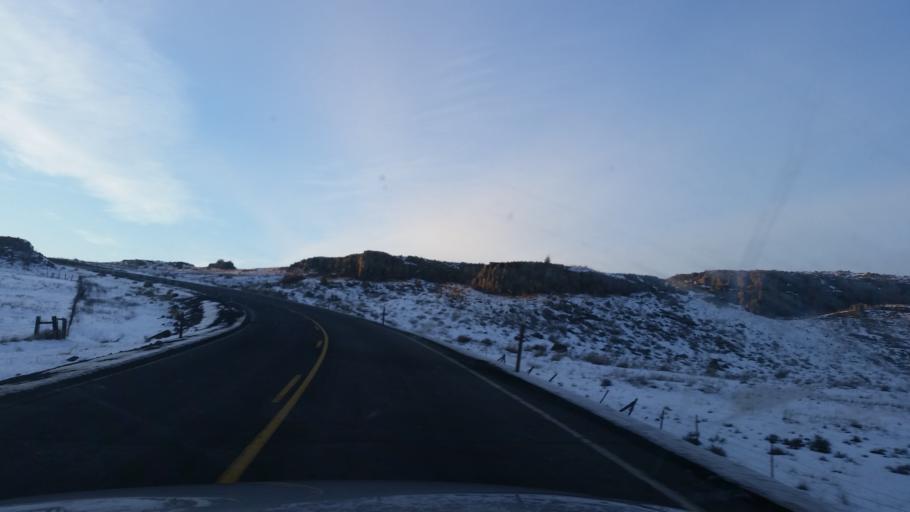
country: US
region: Washington
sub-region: Spokane County
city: Cheney
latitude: 47.1253
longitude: -117.7522
